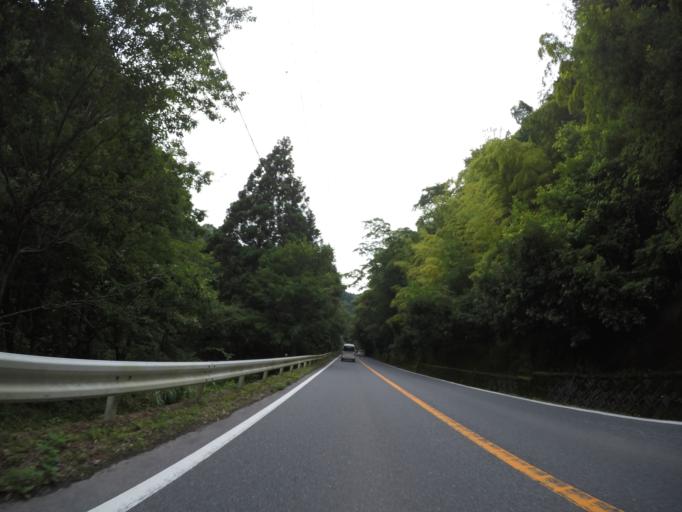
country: JP
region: Shizuoka
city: Fujinomiya
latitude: 35.1967
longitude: 138.5347
